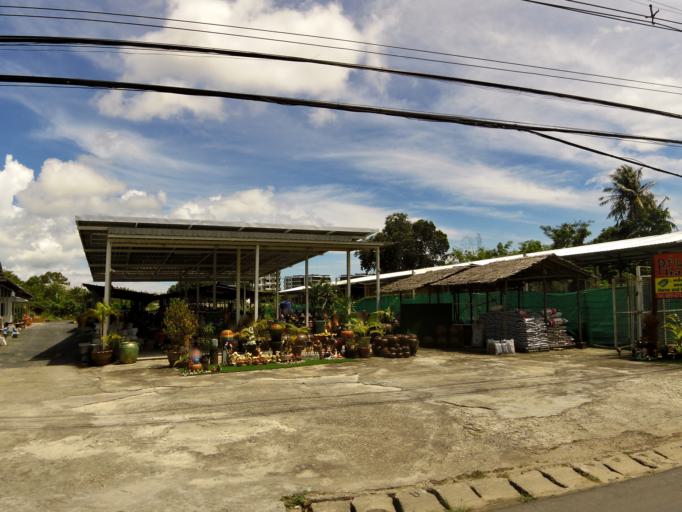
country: TH
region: Phuket
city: Ban Chalong
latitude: 7.8558
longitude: 98.3382
